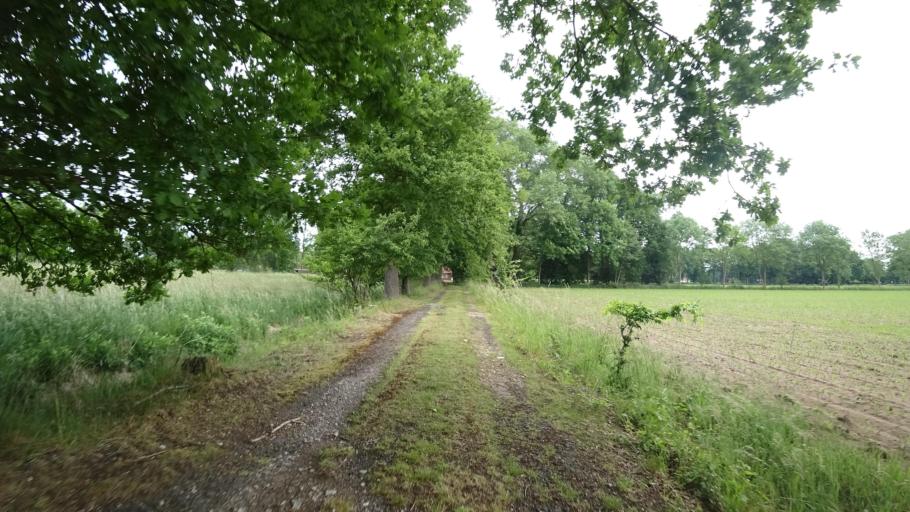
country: DE
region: North Rhine-Westphalia
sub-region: Regierungsbezirk Detmold
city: Guetersloh
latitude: 51.9153
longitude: 8.3353
